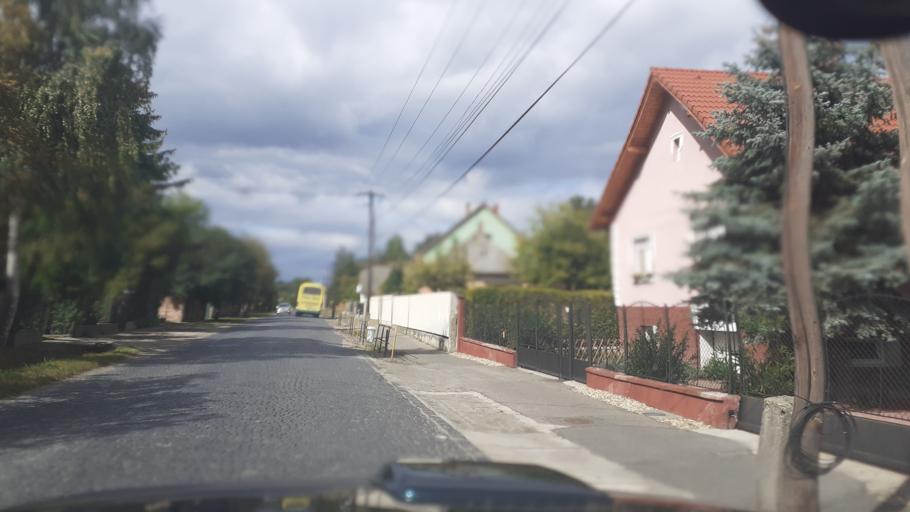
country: HU
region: Bacs-Kiskun
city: Solt
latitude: 46.8040
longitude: 18.9961
